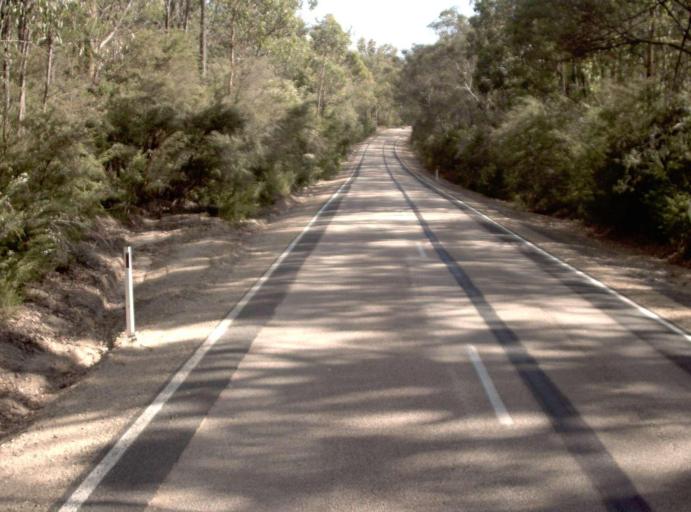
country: AU
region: Victoria
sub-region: East Gippsland
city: Lakes Entrance
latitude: -37.6762
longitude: 148.0552
